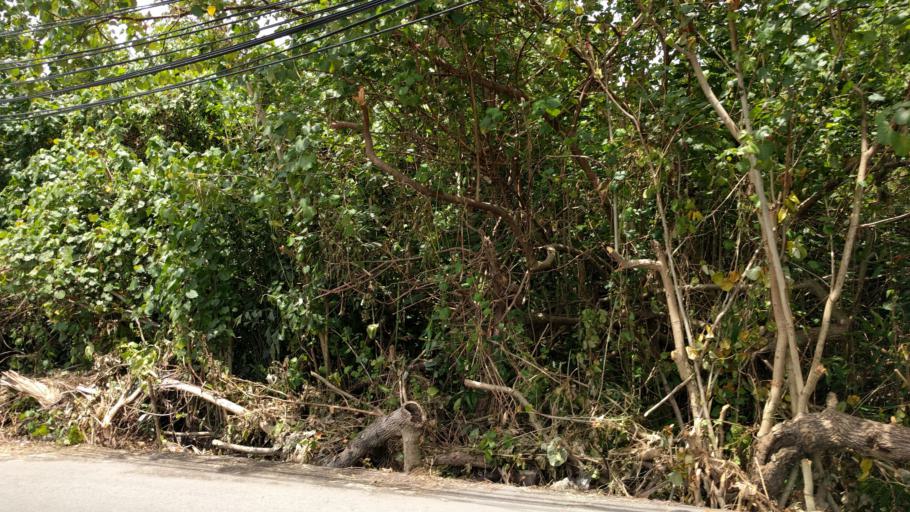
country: ID
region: Bali
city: Banjar Gunungpande
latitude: -8.6702
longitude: 115.1466
